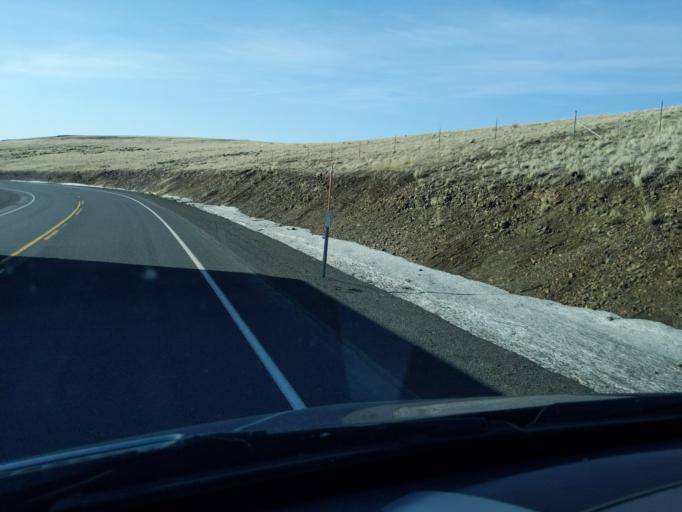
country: US
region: Oregon
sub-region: Umatilla County
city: Pilot Rock
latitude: 45.3004
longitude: -118.9960
